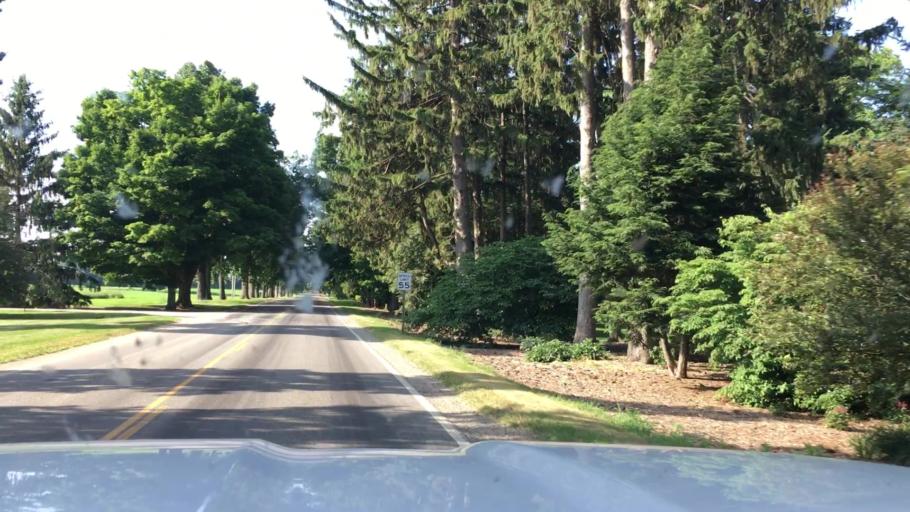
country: US
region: Michigan
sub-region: Kalamazoo County
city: South Gull Lake
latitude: 42.4273
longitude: -85.4546
